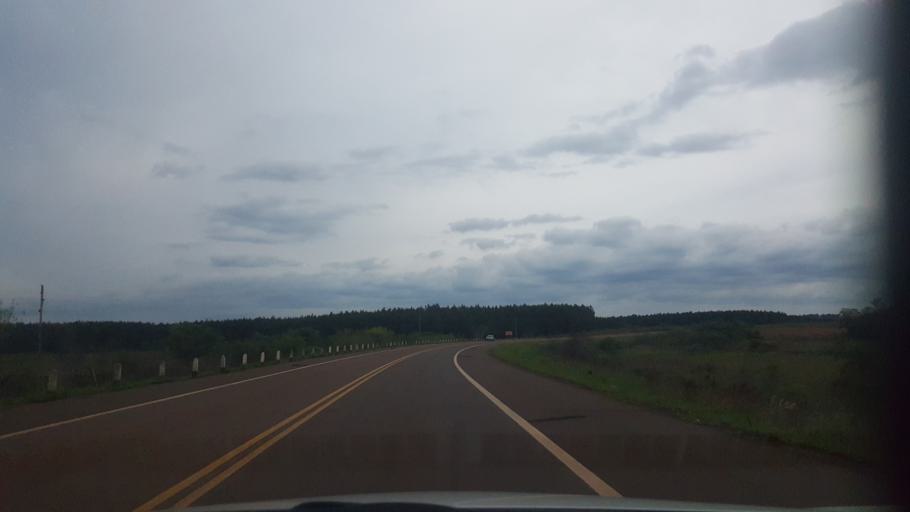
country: AR
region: Misiones
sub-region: Departamento de Candelaria
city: Candelaria
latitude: -27.4918
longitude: -55.7390
